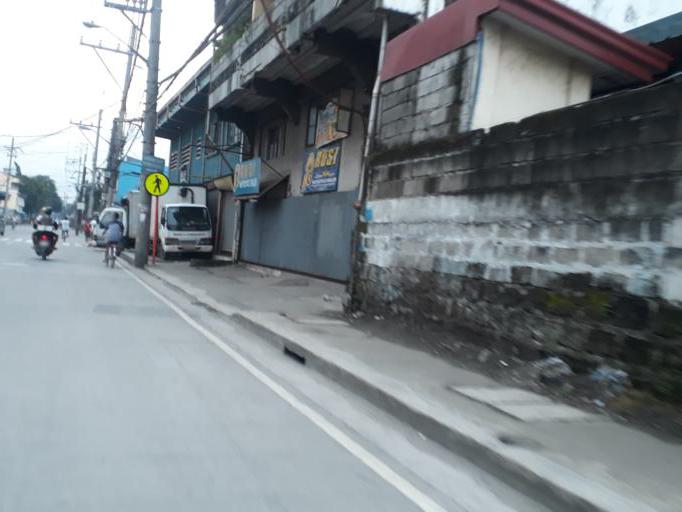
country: PH
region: Calabarzon
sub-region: Province of Rizal
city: Valenzuela
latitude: 14.7000
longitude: 120.9512
